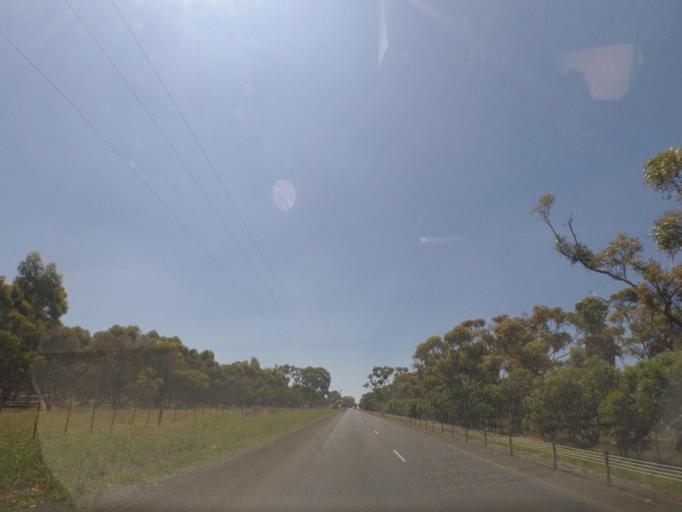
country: AU
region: Victoria
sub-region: Hume
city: Greenvale
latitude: -37.5870
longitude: 144.8560
